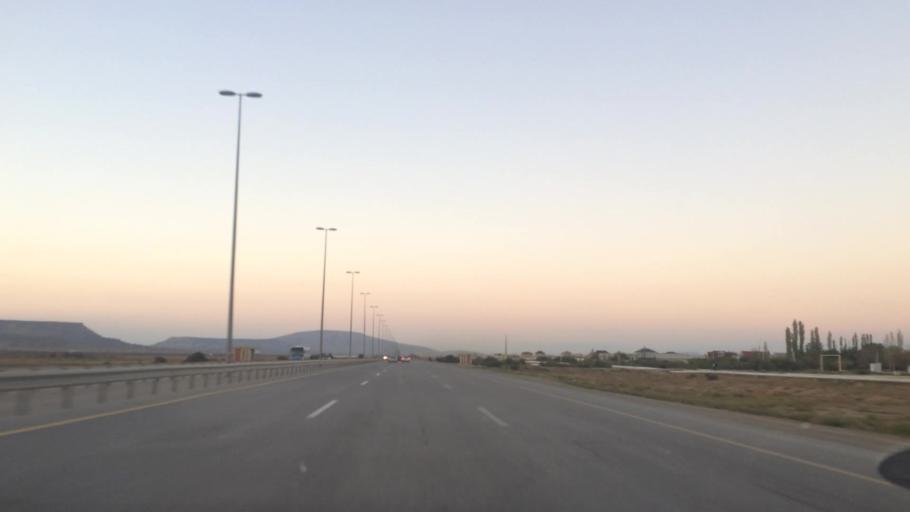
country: AZ
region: Baki
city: Qobustan
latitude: 40.0228
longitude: 49.4245
